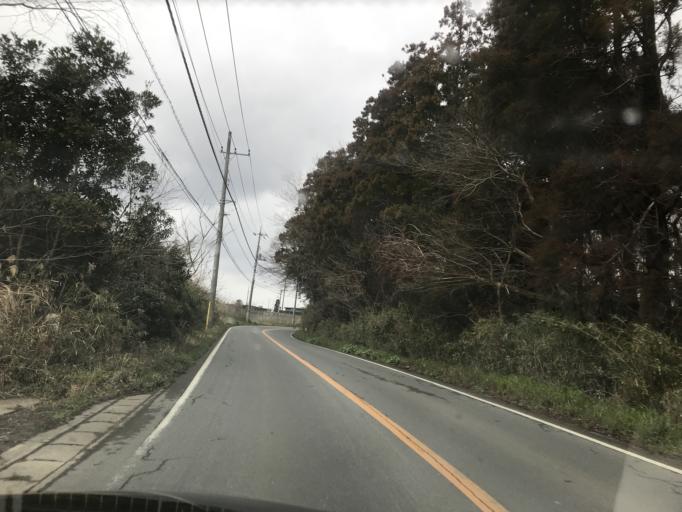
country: JP
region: Chiba
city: Sawara
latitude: 35.8401
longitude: 140.5057
